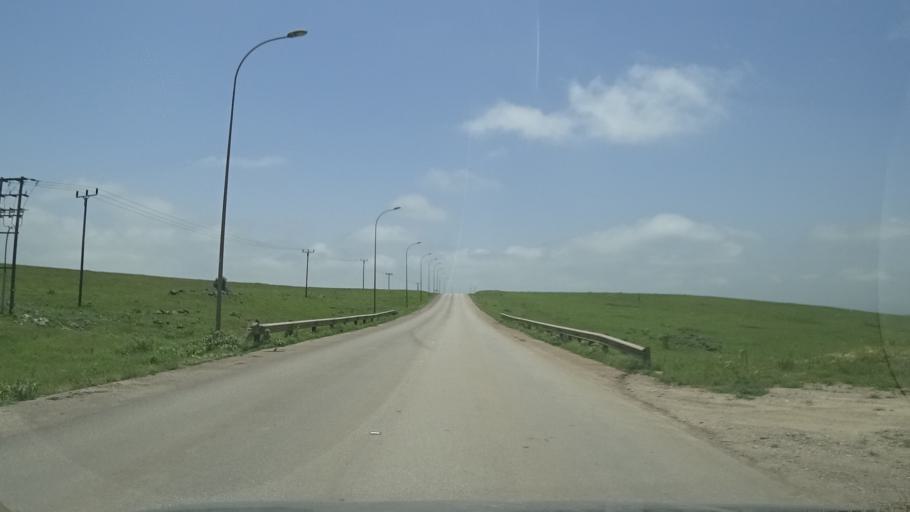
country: OM
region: Zufar
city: Salalah
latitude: 17.2362
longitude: 54.2822
